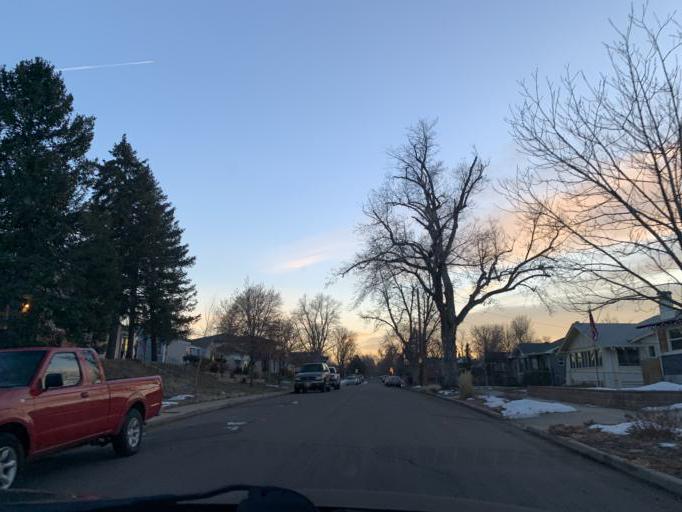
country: US
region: Colorado
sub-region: Adams County
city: Berkley
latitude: 39.7817
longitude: -105.0405
